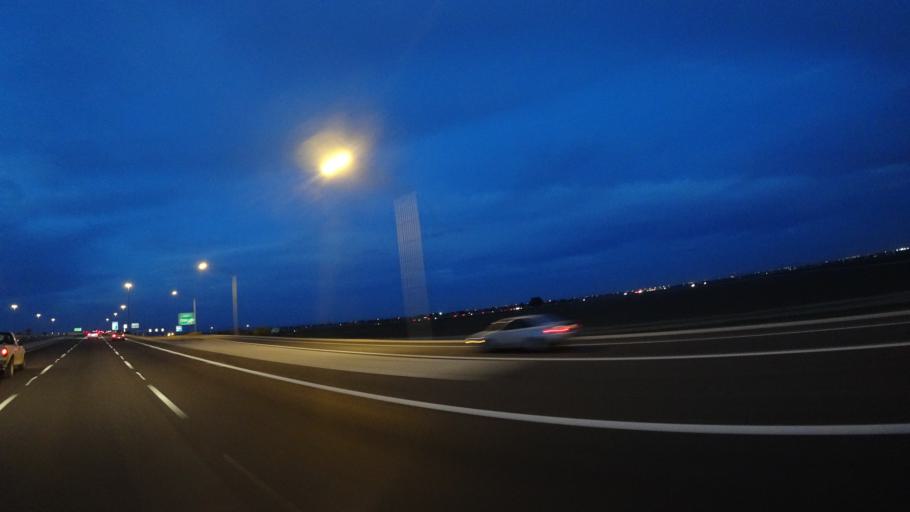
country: US
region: Arizona
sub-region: Maricopa County
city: Citrus Park
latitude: 33.6056
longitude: -112.4179
